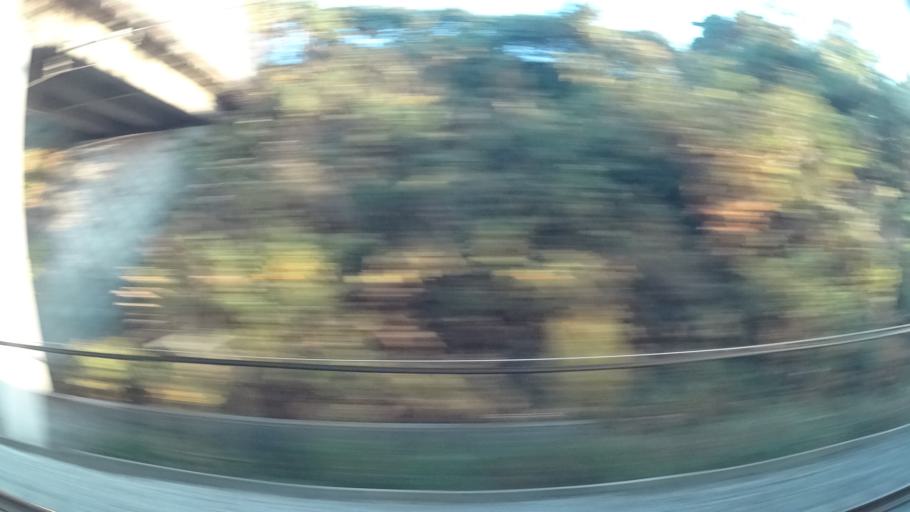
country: JP
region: Shizuoka
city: Numazu
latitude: 35.1460
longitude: 138.7952
